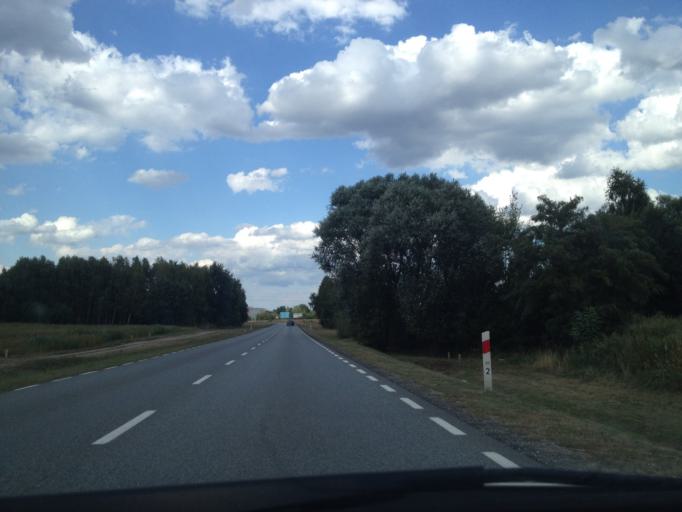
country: PL
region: Lubusz
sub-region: Powiat zarski
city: Zary
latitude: 51.6224
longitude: 15.1119
